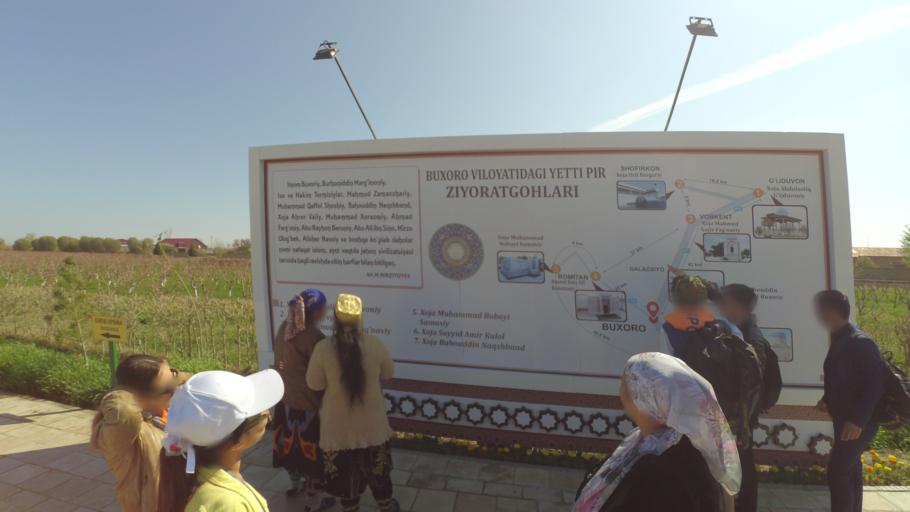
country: UZ
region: Bukhara
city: Kogon
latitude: 39.8018
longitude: 64.5386
